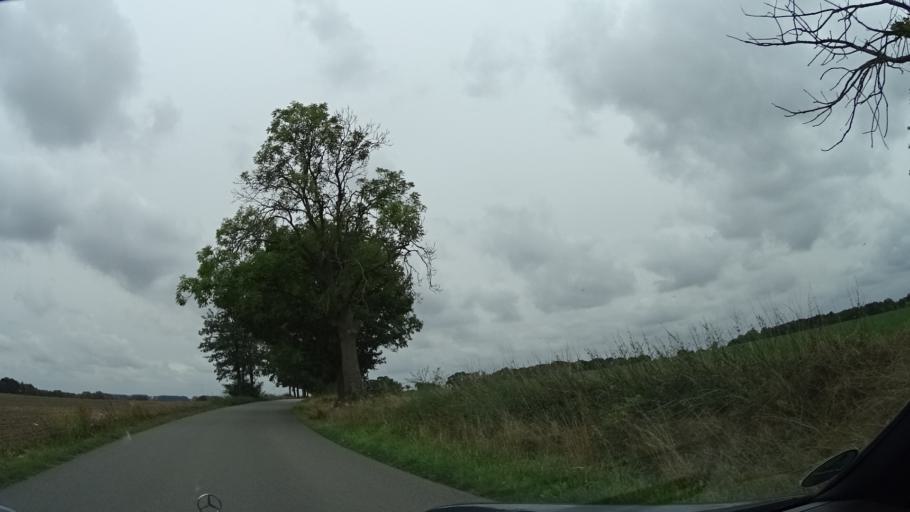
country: DE
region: Brandenburg
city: Neuruppin
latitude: 52.9543
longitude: 12.7621
